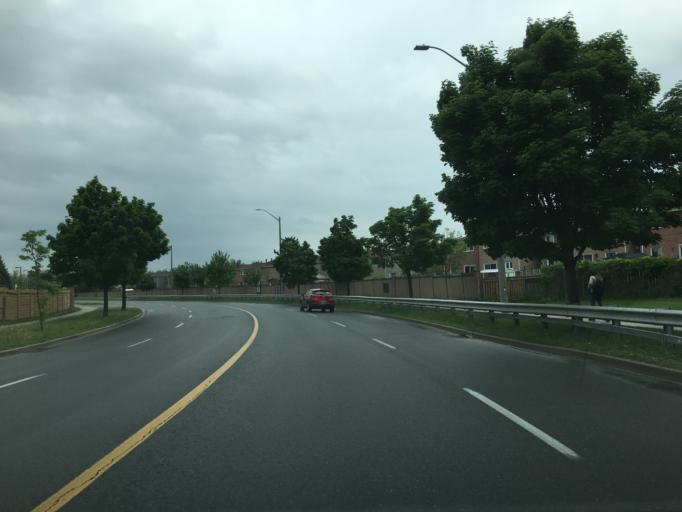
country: CA
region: Ontario
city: Markham
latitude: 43.8358
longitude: -79.2683
